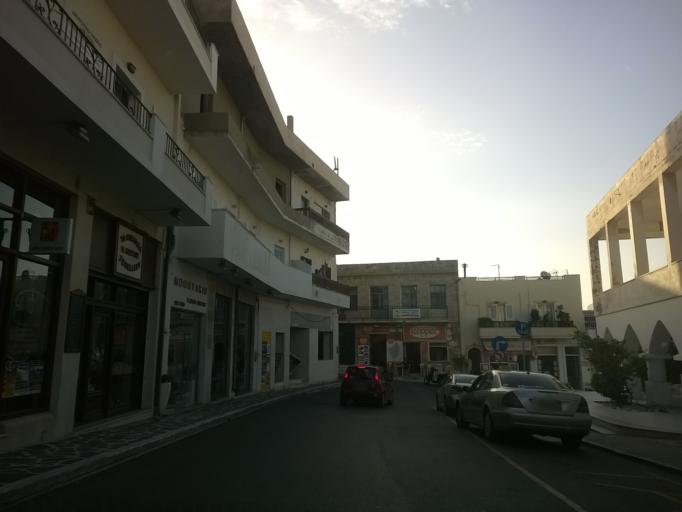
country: GR
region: South Aegean
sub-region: Nomos Kykladon
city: Naxos
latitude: 37.1032
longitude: 25.3755
